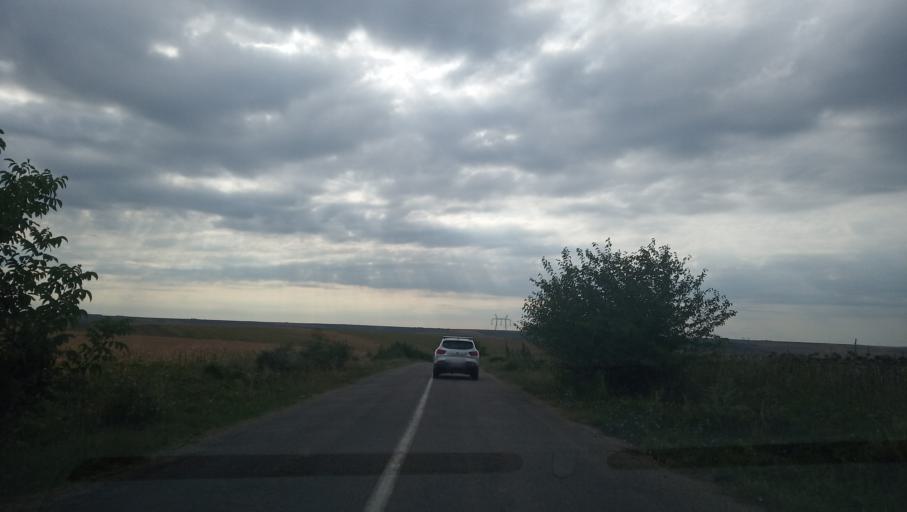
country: RO
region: Constanta
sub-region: Comuna Adamclisi
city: Adamclisi
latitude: 44.0281
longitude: 27.9816
